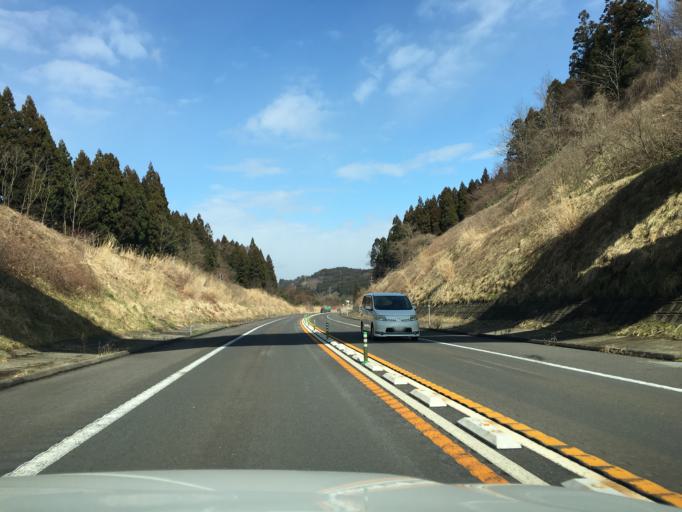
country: JP
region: Akita
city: Akita
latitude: 39.7682
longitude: 140.1220
